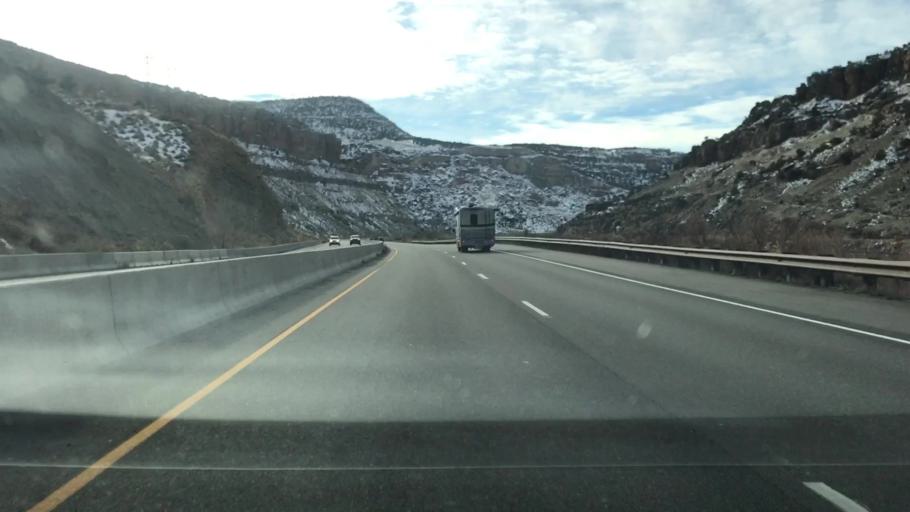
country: US
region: Colorado
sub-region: Mesa County
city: Palisade
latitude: 39.2181
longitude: -108.2564
